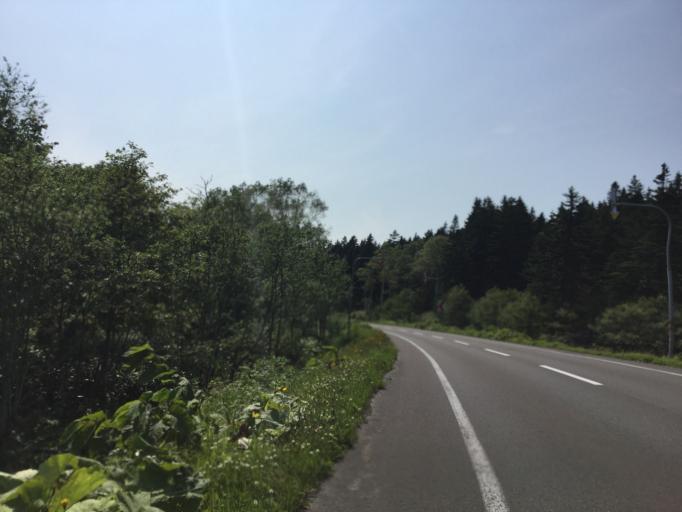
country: JP
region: Hokkaido
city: Makubetsu
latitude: 45.4119
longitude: 141.9742
